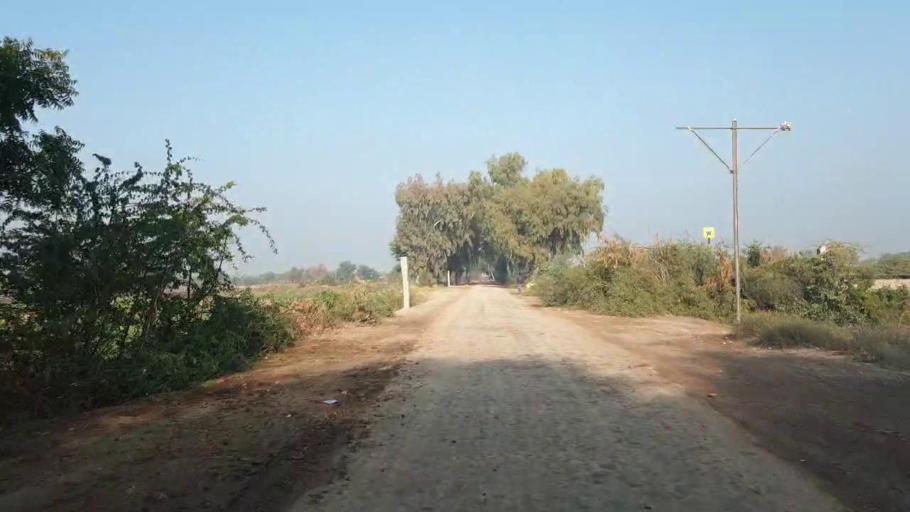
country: PK
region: Sindh
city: Shahdadpur
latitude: 25.9675
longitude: 68.6090
